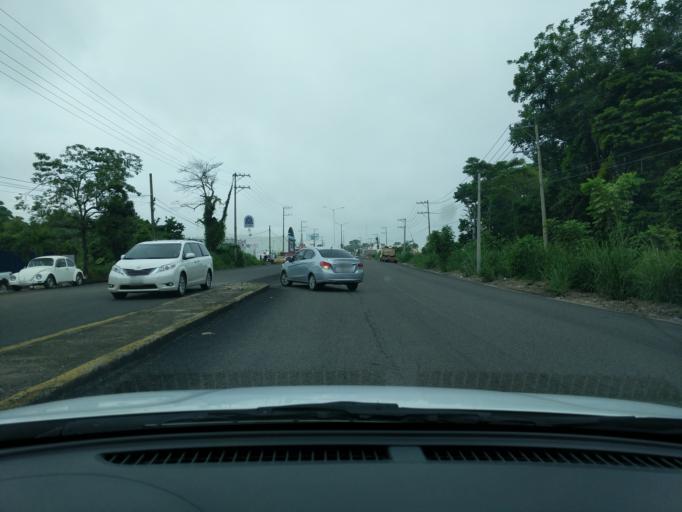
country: MX
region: Tabasco
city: Villahermosa
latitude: 17.9602
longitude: -92.9658
